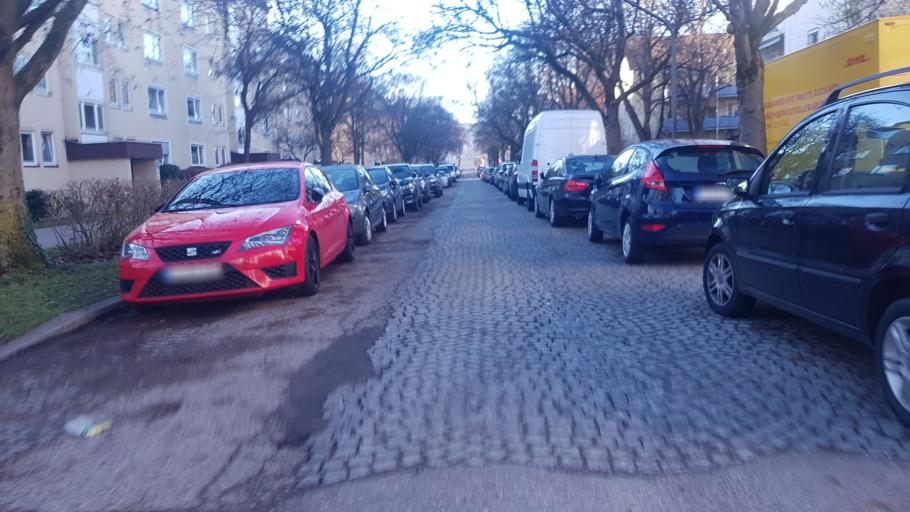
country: DE
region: Bavaria
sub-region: Upper Bavaria
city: Pasing
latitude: 48.1478
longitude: 11.5061
